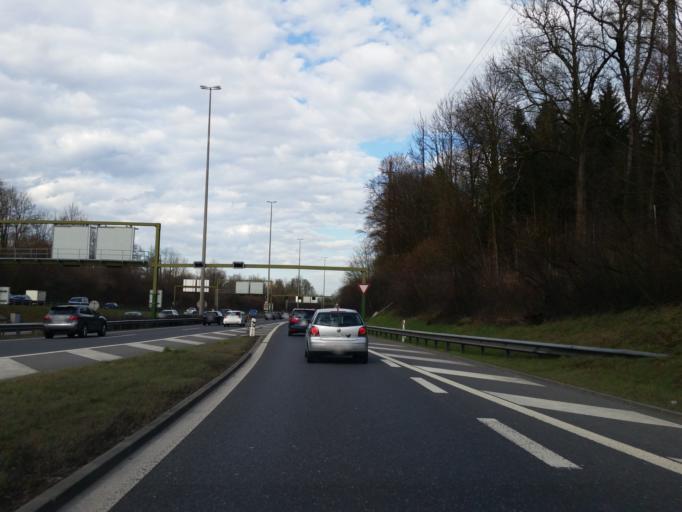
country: CH
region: Lucerne
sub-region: Hochdorf District
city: Emmen
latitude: 47.0719
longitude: 8.2998
